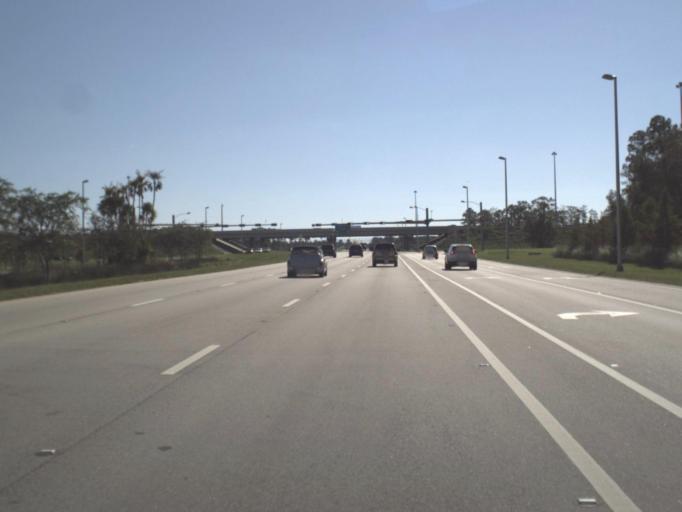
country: US
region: Florida
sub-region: Lee County
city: Fort Myers
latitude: 26.6359
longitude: -81.8063
